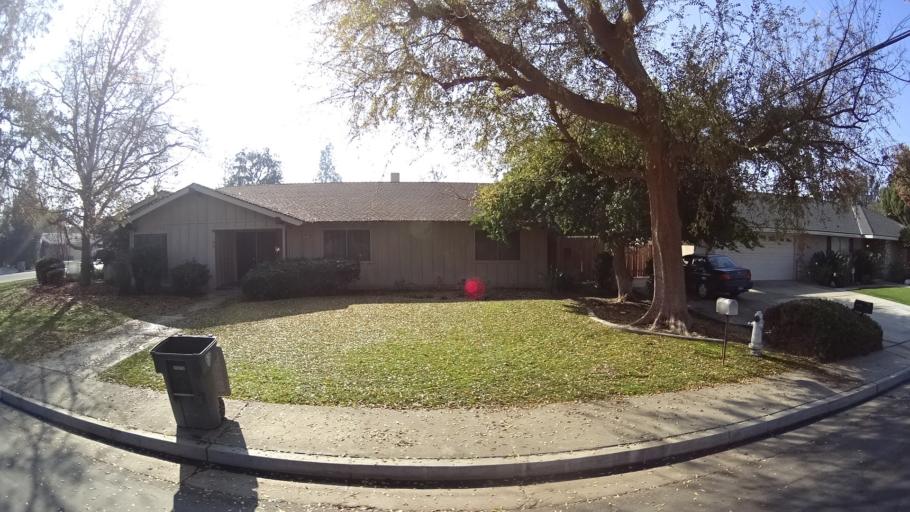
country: US
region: California
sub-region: Kern County
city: Greenacres
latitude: 35.3524
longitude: -119.0824
